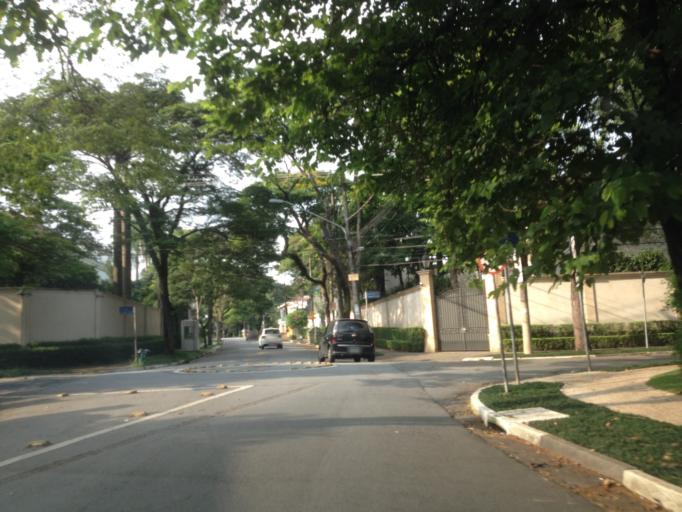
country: BR
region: Sao Paulo
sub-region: Sao Paulo
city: Sao Paulo
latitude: -23.5771
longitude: -46.6765
